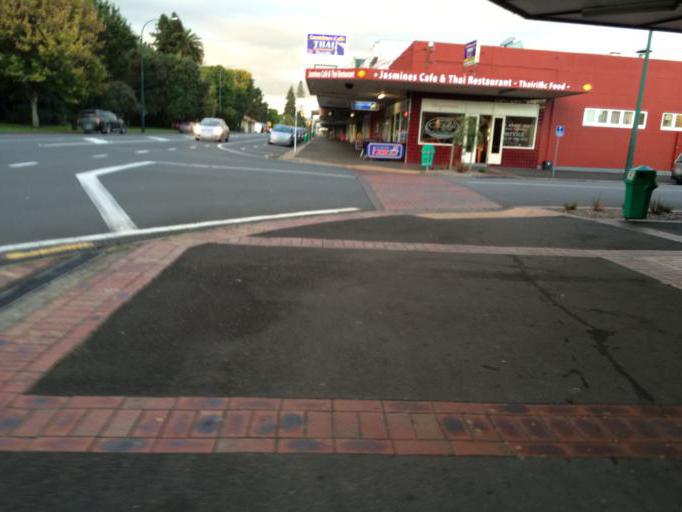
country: NZ
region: Waikato
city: Turangi
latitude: -38.8832
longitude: 175.2606
